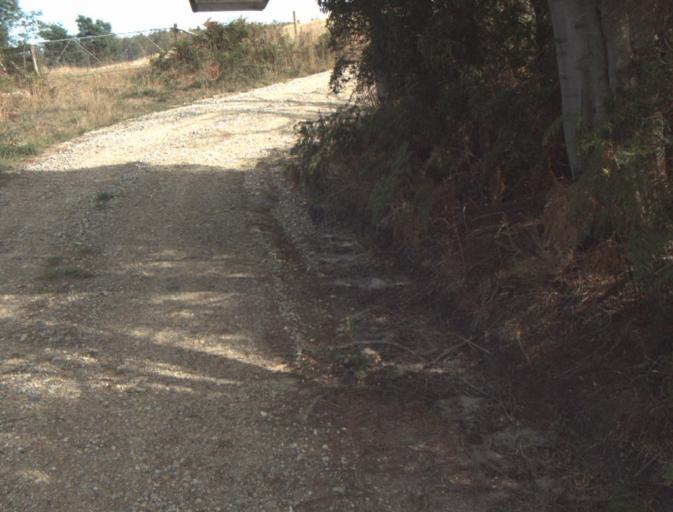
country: AU
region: Tasmania
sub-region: Launceston
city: Mayfield
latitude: -41.1903
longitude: 147.2213
